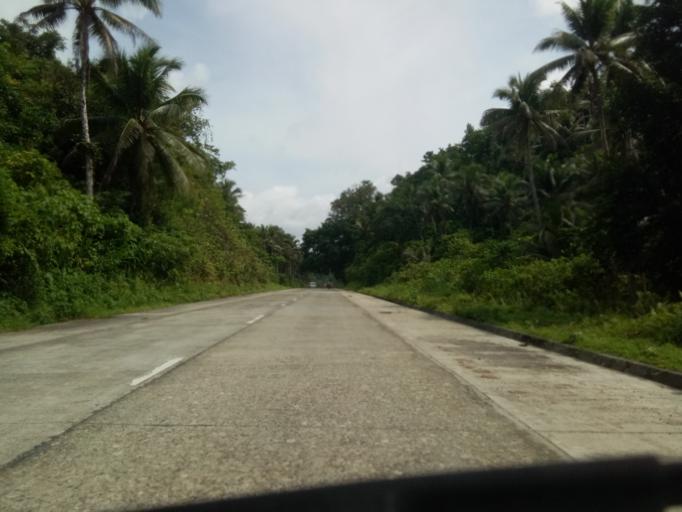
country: PH
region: Caraga
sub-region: Province of Surigao del Norte
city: Dapa
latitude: 9.7955
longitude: 126.0706
